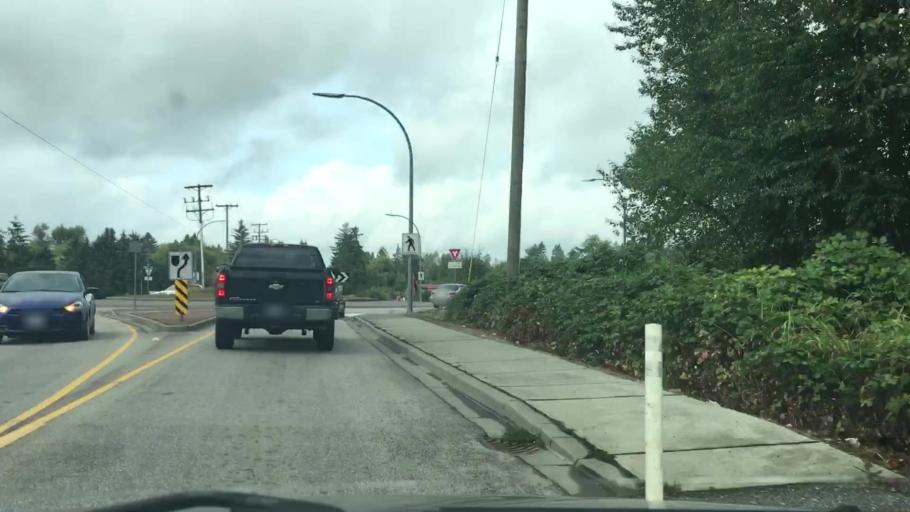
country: CA
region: British Columbia
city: Langley
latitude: 49.1040
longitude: -122.5804
